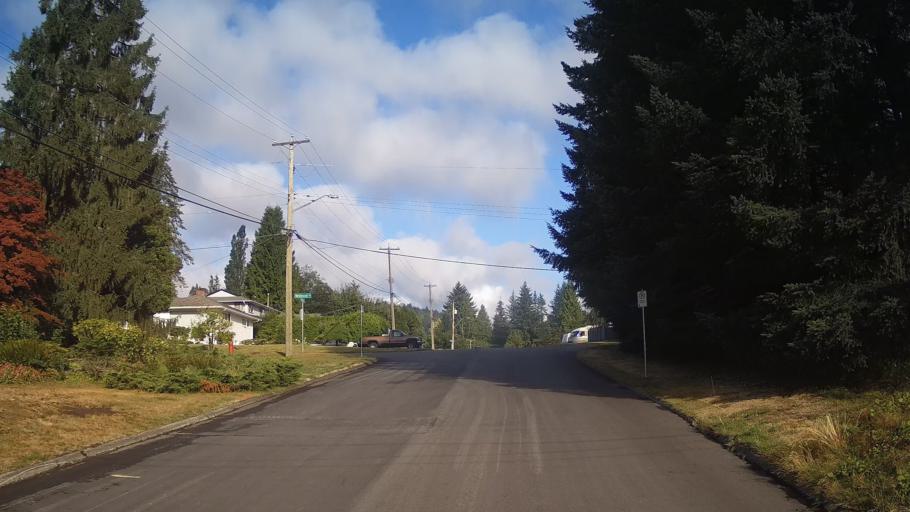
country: CA
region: British Columbia
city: Port Moody
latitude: 49.2741
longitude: -122.8773
